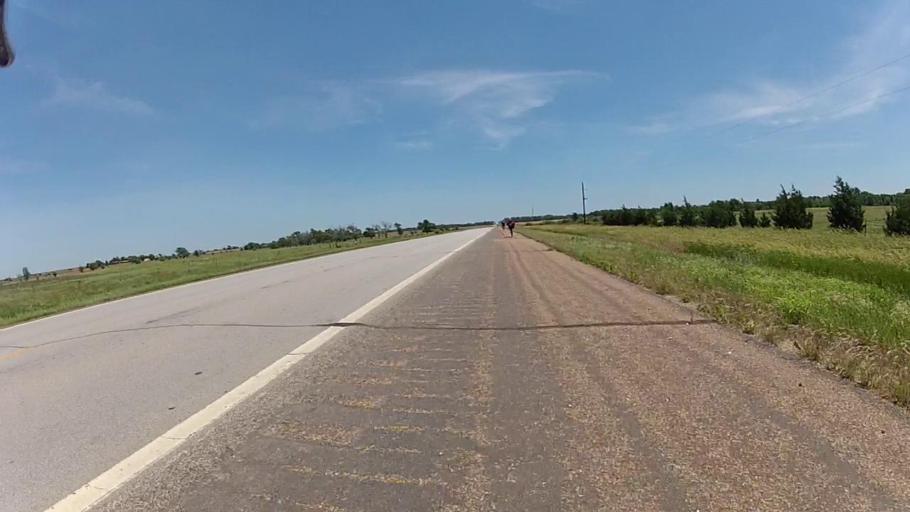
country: US
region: Kansas
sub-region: Barber County
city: Medicine Lodge
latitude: 37.2533
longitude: -98.3184
